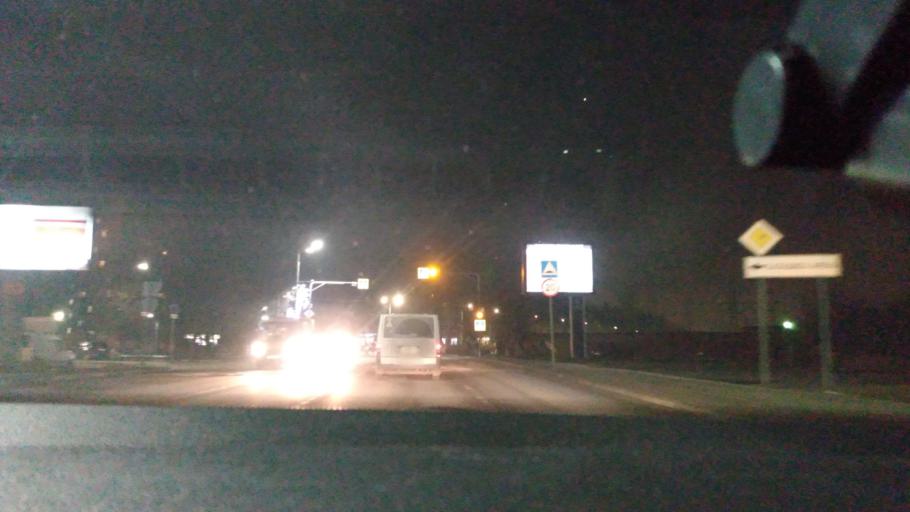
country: RU
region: Moskovskaya
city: Balashikha
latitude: 55.8052
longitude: 37.9391
